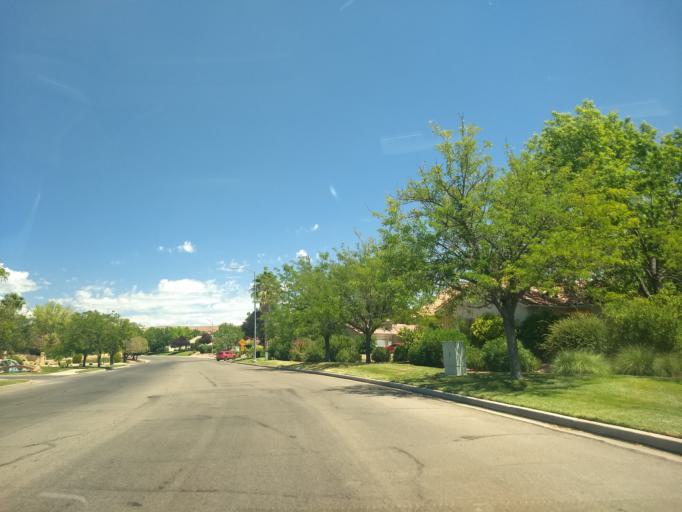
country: US
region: Utah
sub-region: Washington County
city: Washington
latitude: 37.1393
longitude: -113.5251
